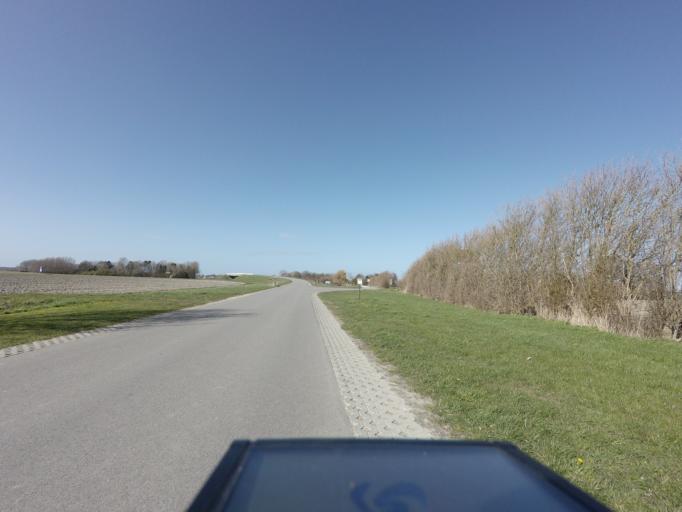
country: NL
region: Zeeland
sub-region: Schouwen-Duiveland
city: Scharendijke
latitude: 51.7215
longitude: 3.8234
